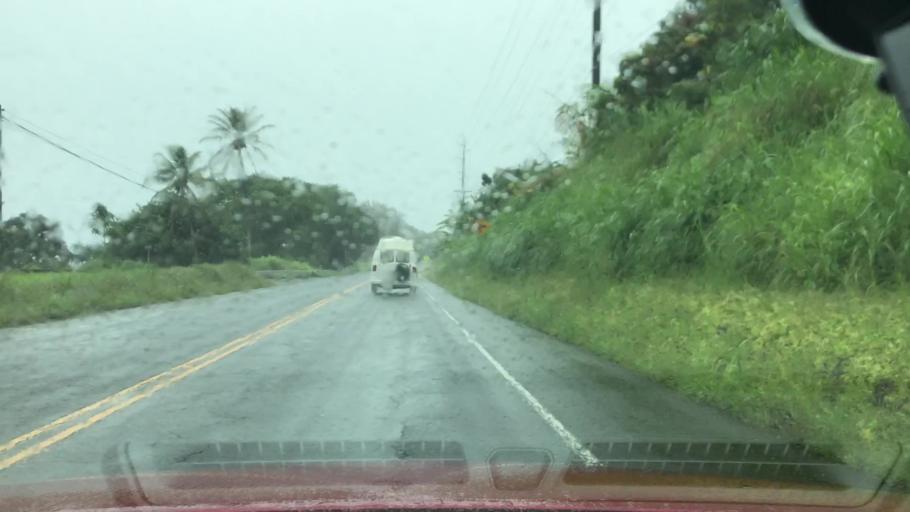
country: US
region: Hawaii
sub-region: Hawaii County
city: Pepeekeo
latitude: 19.9852
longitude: -155.2364
